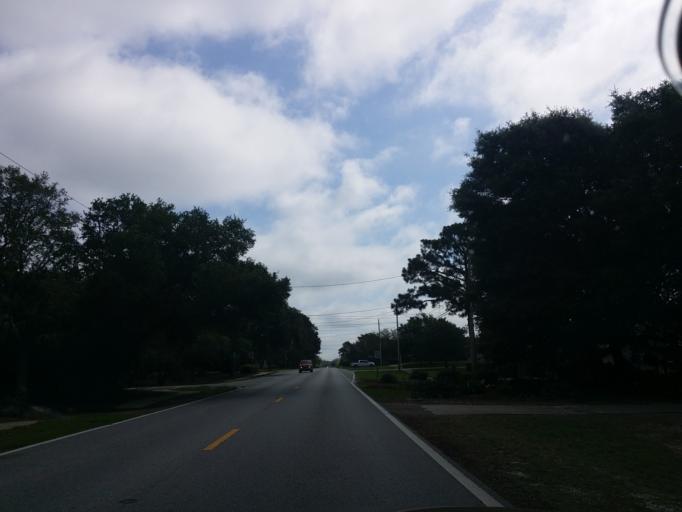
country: US
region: Florida
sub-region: Santa Rosa County
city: Gulf Breeze
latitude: 30.3618
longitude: -87.1778
